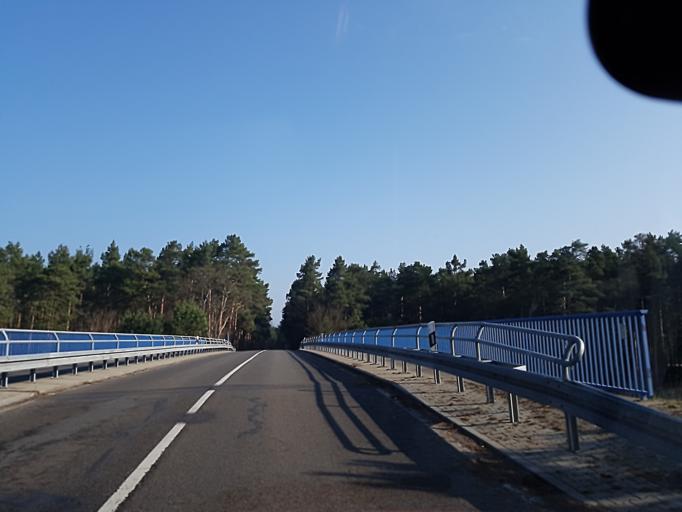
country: PL
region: Lubusz
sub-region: Powiat zarski
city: Trzebiel
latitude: 51.6660
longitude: 14.7364
